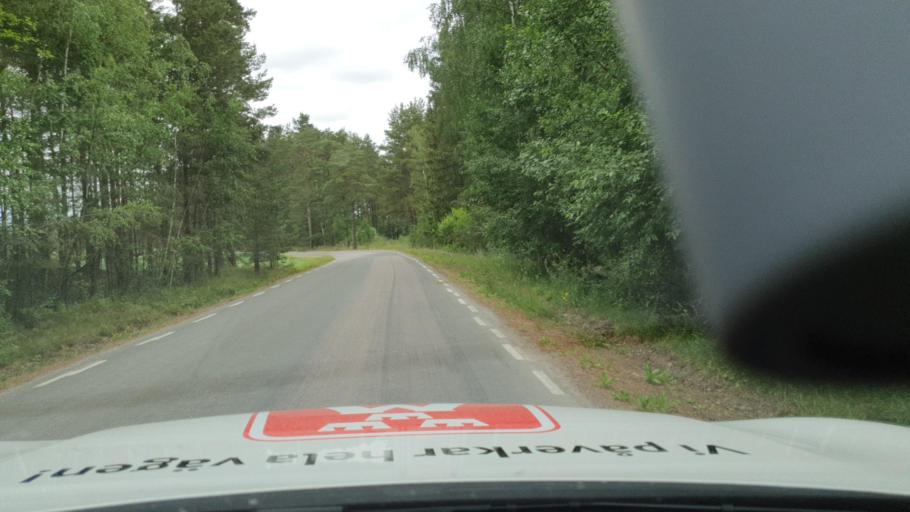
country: SE
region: Vaestra Goetaland
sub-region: Tidaholms Kommun
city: Olofstorp
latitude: 58.2358
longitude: 14.0983
